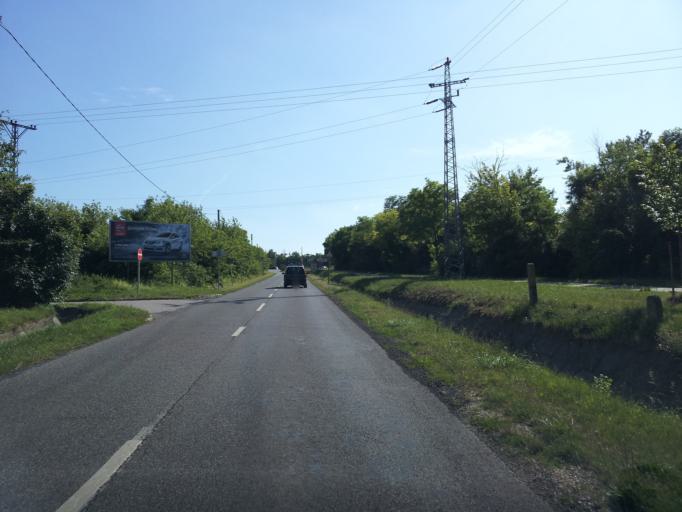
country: HU
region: Veszprem
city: Veszprem
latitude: 47.0811
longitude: 17.8953
